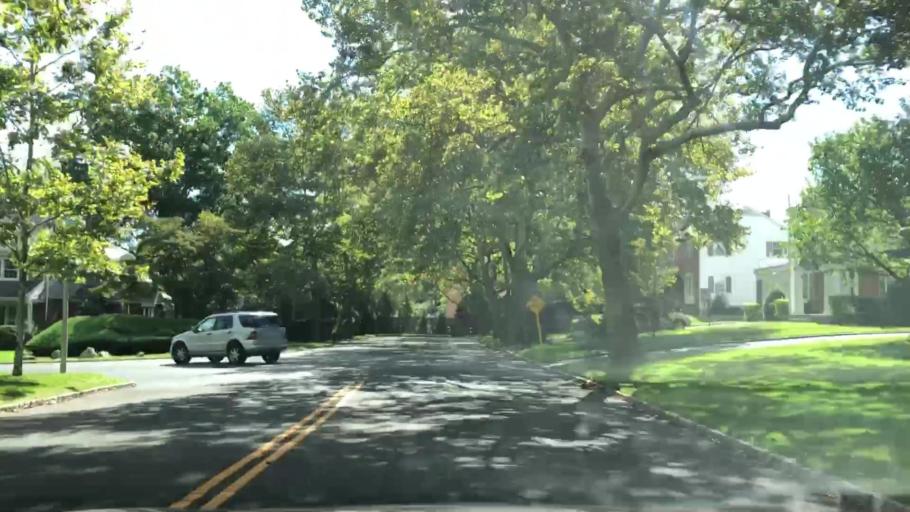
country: US
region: New York
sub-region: Nassau County
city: Munsey Park
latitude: 40.7984
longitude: -73.6718
